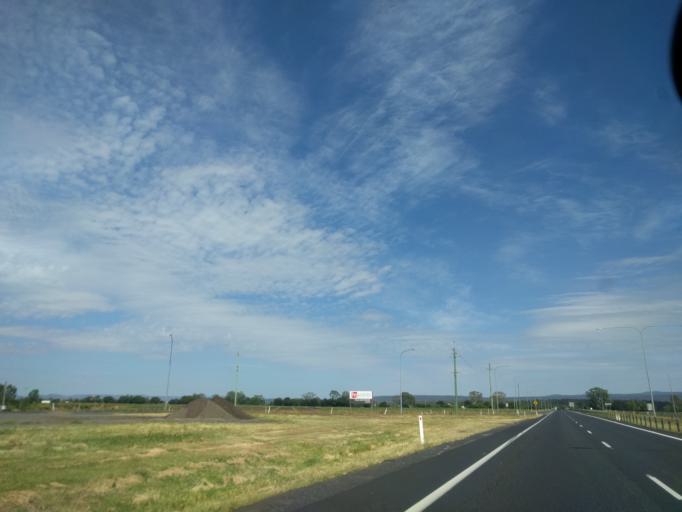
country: AU
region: Queensland
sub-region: Lockyer Valley
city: Gatton
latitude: -27.5490
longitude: 152.3163
